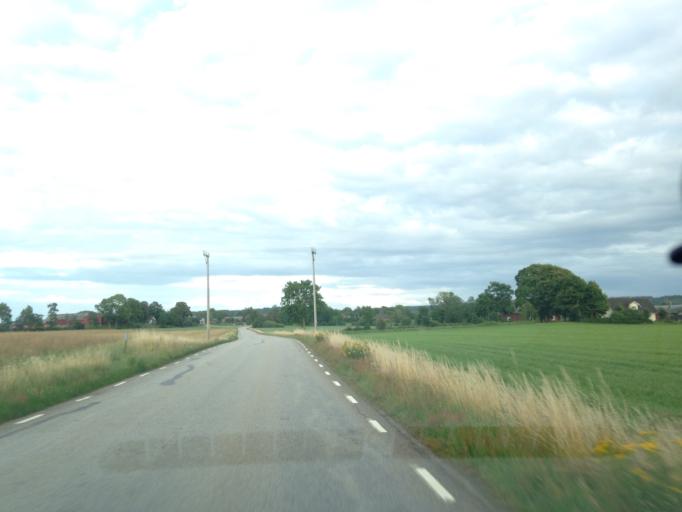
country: SE
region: Halland
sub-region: Varbergs Kommun
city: Tvaaker
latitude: 57.1133
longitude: 12.4100
